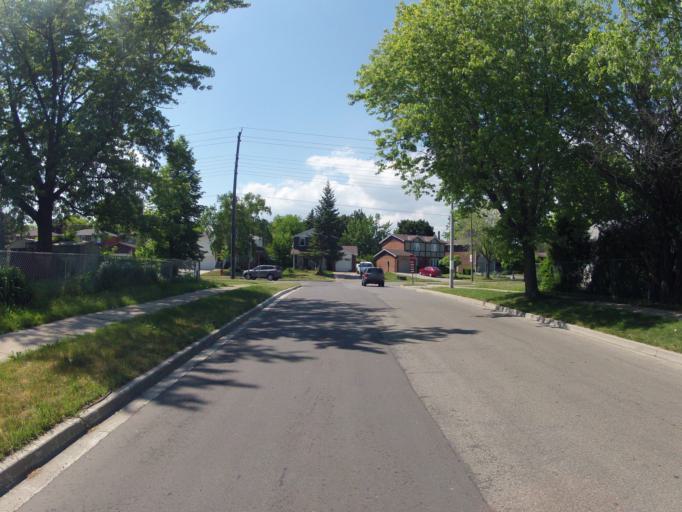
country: CA
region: Ontario
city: Mississauga
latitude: 43.5139
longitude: -79.6526
